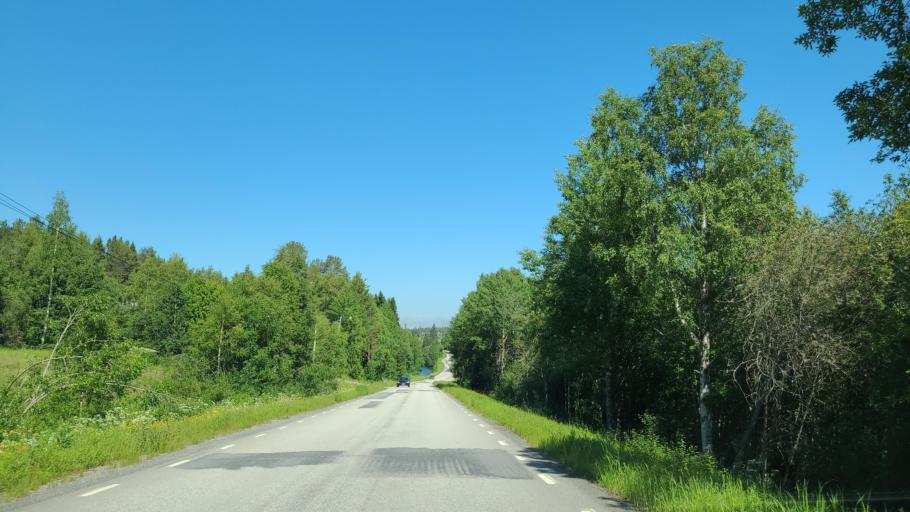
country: SE
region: Vaesternorrland
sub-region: OErnskoeldsviks Kommun
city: Husum
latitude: 63.3768
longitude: 19.1974
